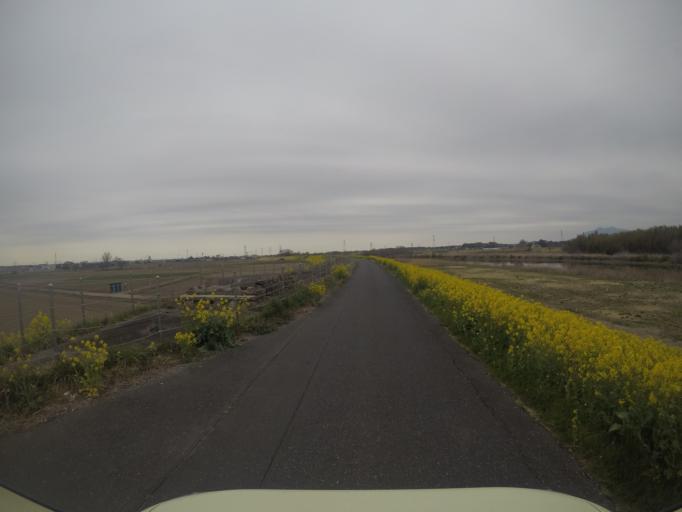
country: JP
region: Ibaraki
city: Ishige
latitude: 36.0983
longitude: 140.0043
